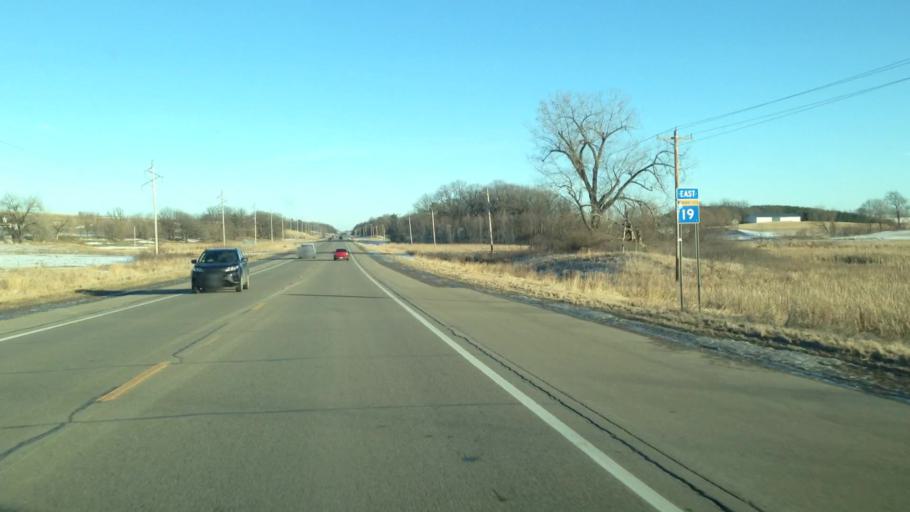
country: US
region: Minnesota
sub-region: Rice County
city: Lonsdale
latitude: 44.4792
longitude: -93.3925
